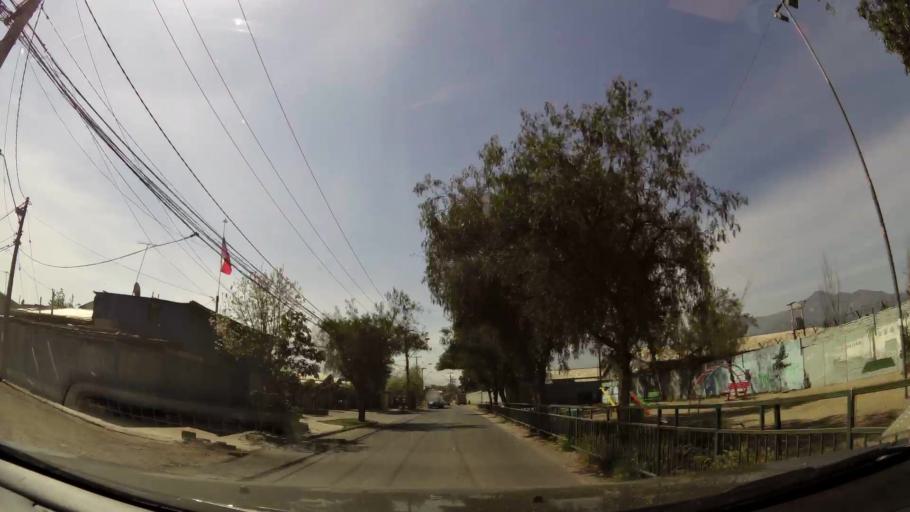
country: CL
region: Santiago Metropolitan
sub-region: Provincia de Cordillera
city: Puente Alto
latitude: -33.6181
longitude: -70.5721
